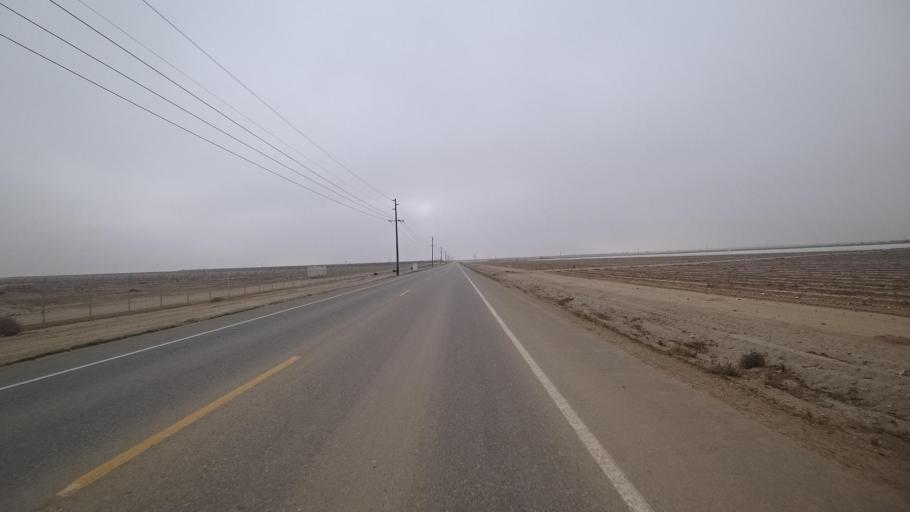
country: US
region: California
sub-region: Kern County
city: Greenfield
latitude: 35.1056
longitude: -119.1097
